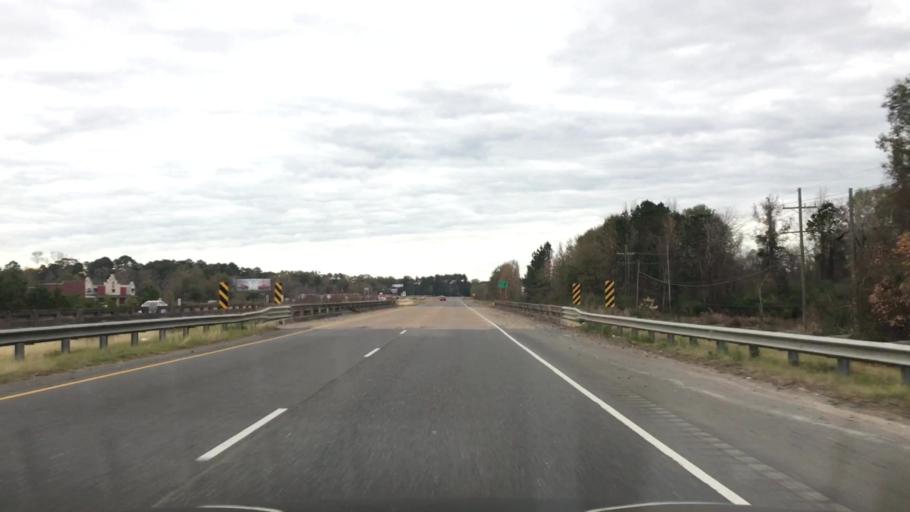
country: US
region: Louisiana
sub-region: Vernon Parish
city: New Llano
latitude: 31.1083
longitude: -93.2710
